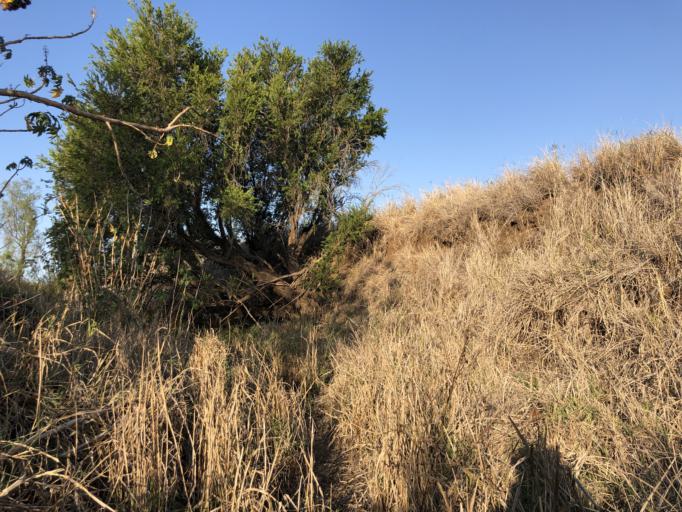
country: AU
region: Queensland
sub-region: Lockyer Valley
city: Gatton
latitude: -27.5844
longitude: 152.3491
